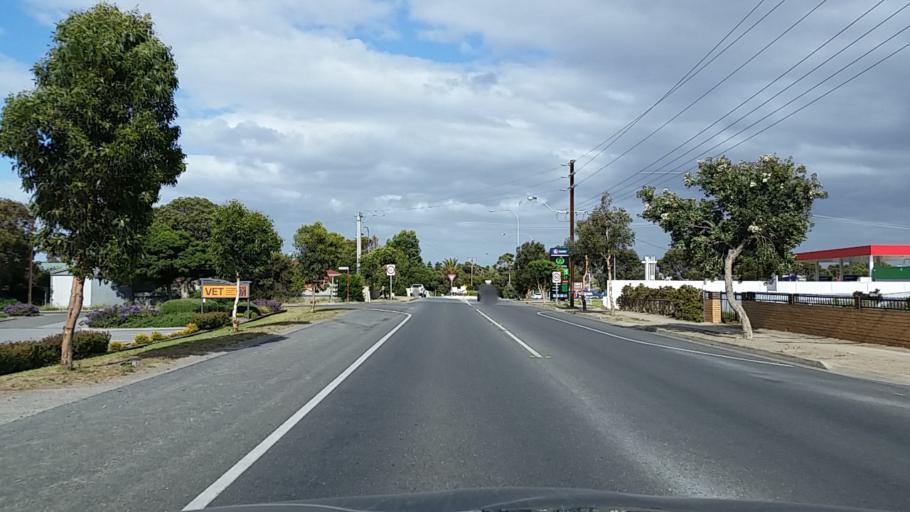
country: AU
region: South Australia
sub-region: Alexandrina
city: Goolwa
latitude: -35.5047
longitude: 138.7754
